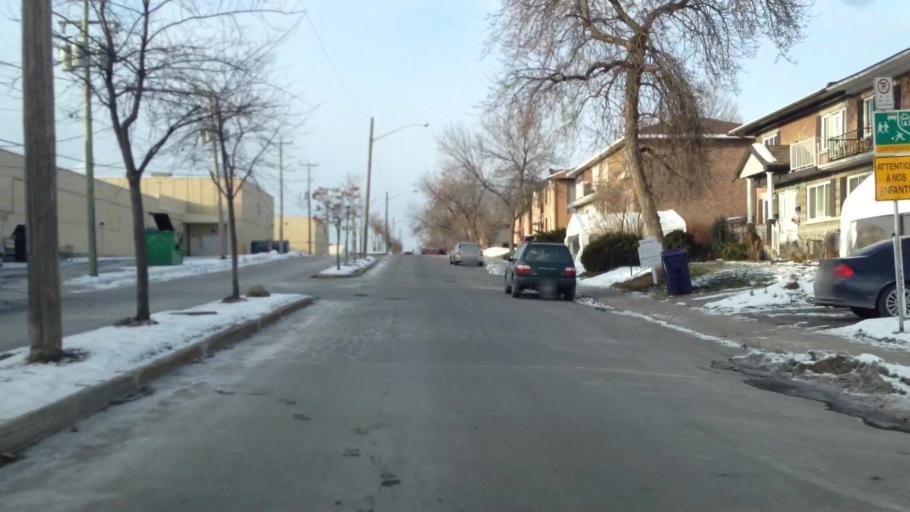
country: CA
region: Quebec
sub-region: Laval
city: Laval
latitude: 45.5421
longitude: -73.7473
